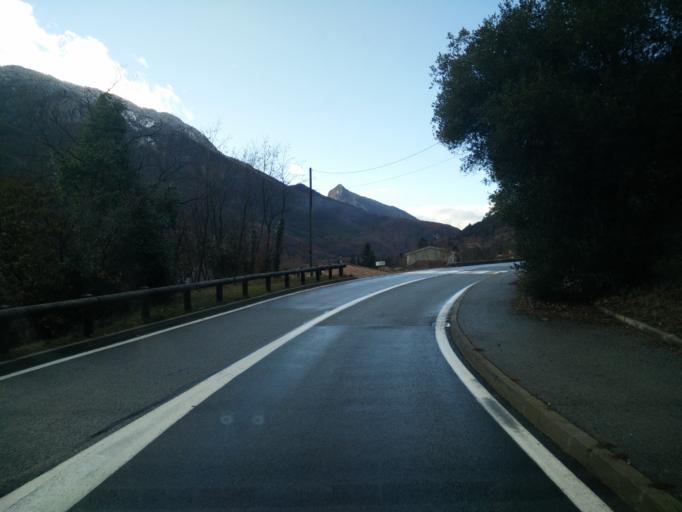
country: FR
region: Provence-Alpes-Cote d'Azur
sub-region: Departement des Alpes-Maritimes
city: Puget-Theniers
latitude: 43.9472
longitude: 7.0140
